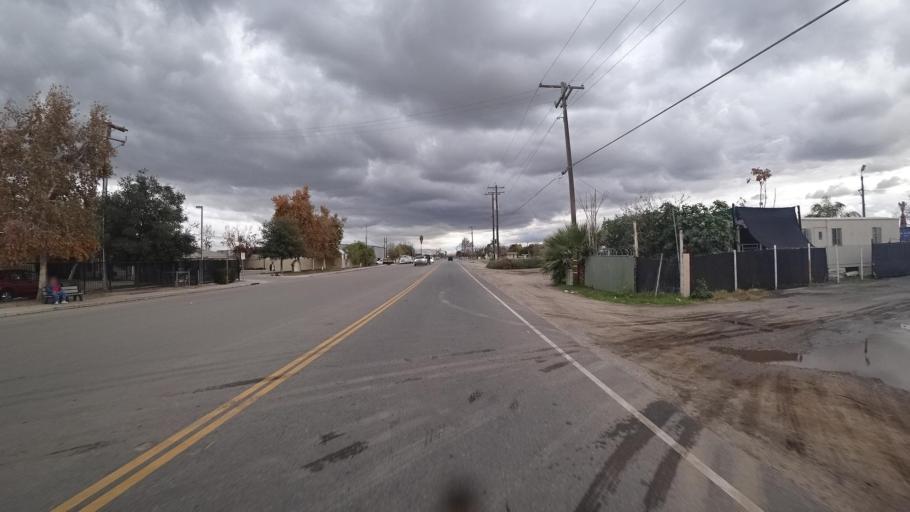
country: US
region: California
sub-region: Kern County
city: Greenfield
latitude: 35.3176
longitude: -119.0014
